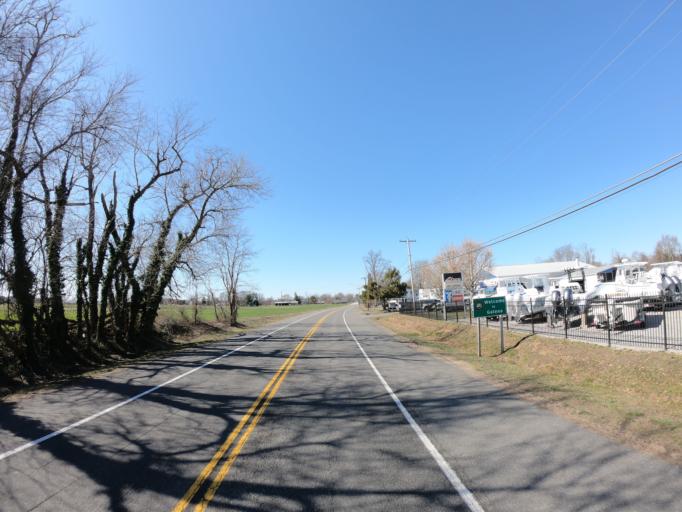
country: US
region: Delaware
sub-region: New Castle County
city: Townsend
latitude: 39.3413
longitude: -75.8730
